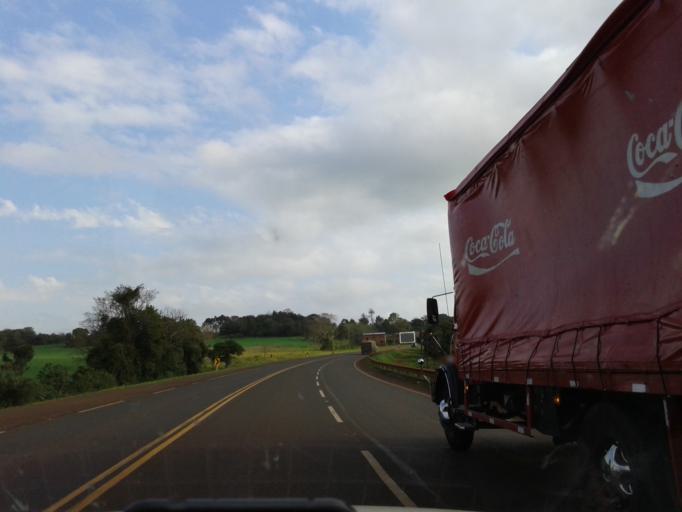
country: PY
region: Itapua
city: Edelira
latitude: -26.7186
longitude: -55.3320
